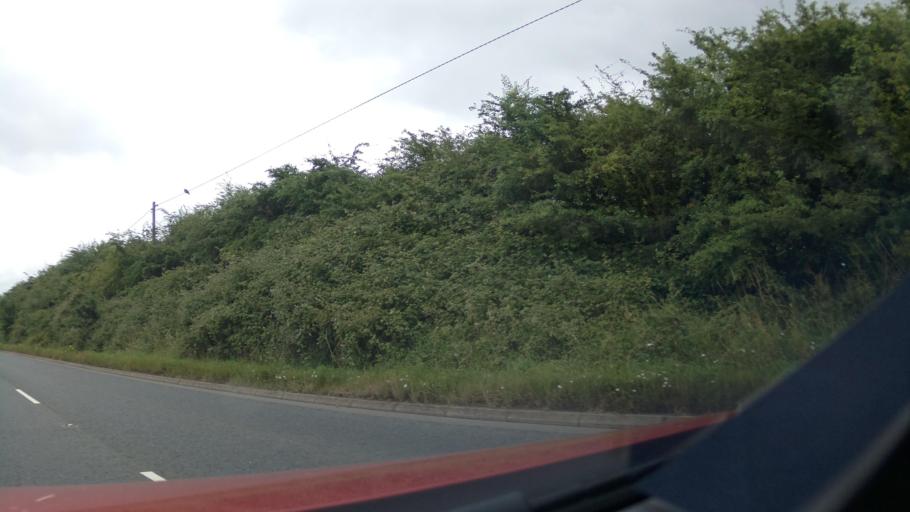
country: GB
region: England
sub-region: Worcestershire
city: Fernhill Heath
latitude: 52.2316
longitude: -2.1705
